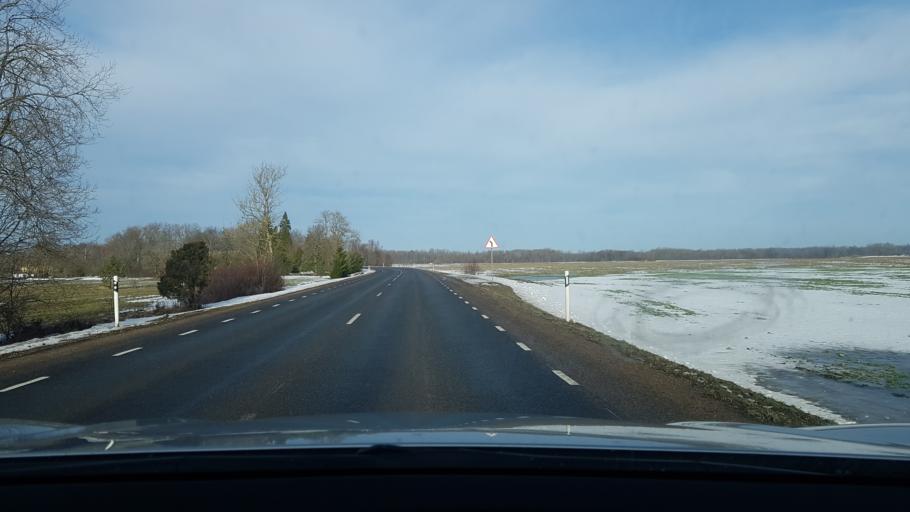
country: EE
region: Saare
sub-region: Kuressaare linn
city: Kuressaare
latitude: 58.2933
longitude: 22.5414
